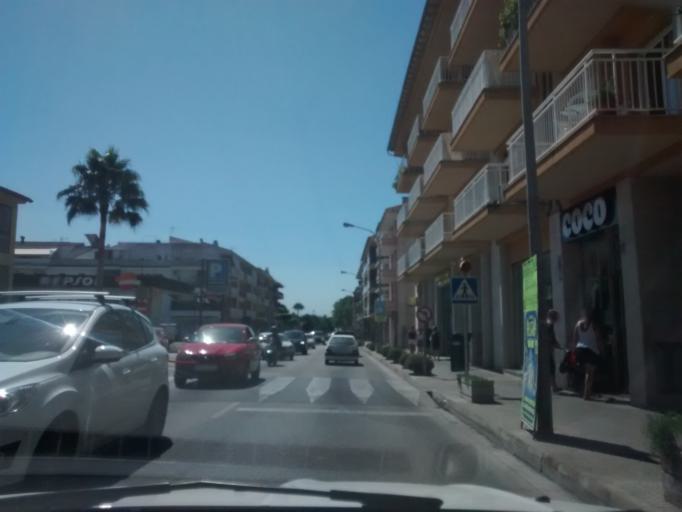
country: ES
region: Balearic Islands
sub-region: Illes Balears
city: Alcudia
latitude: 39.8504
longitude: 3.1267
